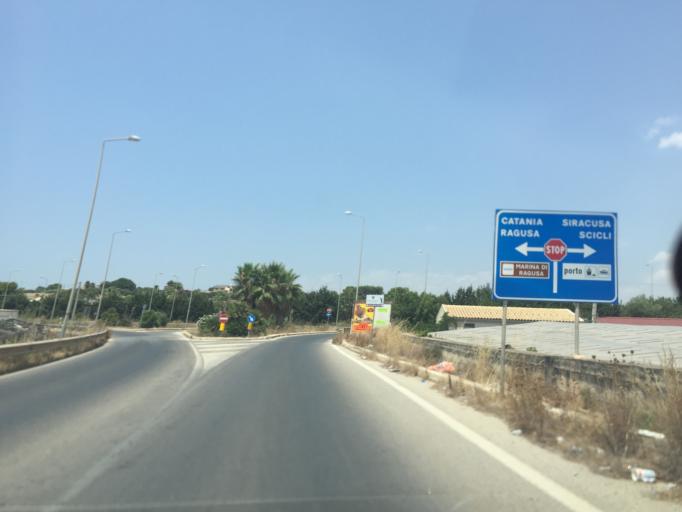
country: IT
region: Sicily
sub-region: Ragusa
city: Donnalucata
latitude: 36.7754
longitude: 14.6082
